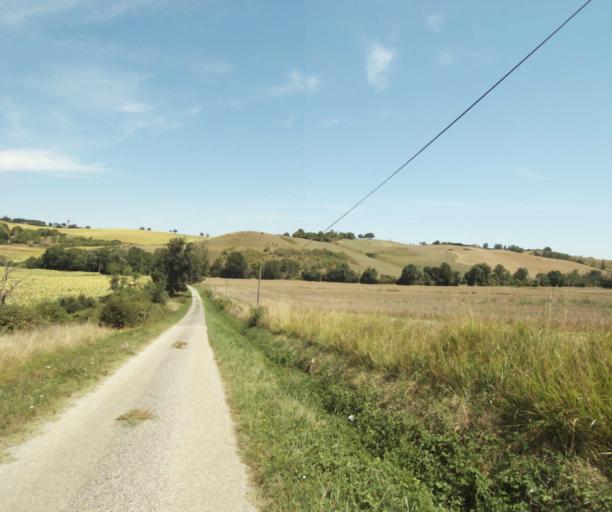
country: FR
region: Midi-Pyrenees
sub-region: Departement de l'Ariege
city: Lezat-sur-Leze
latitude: 43.2699
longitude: 1.2997
